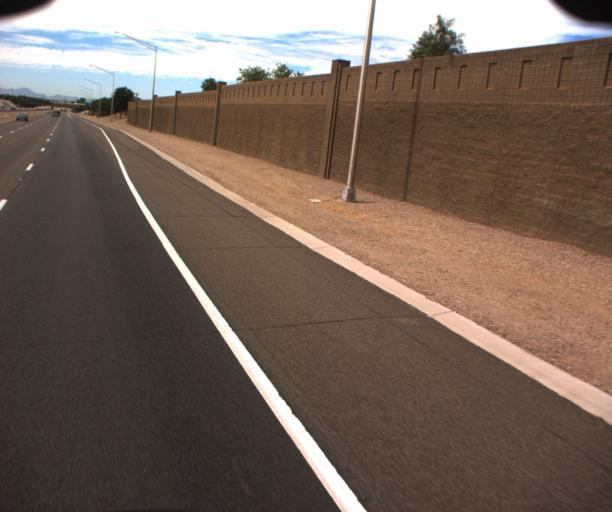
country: US
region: Arizona
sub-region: Maricopa County
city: Gilbert
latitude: 33.3285
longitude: -111.7111
